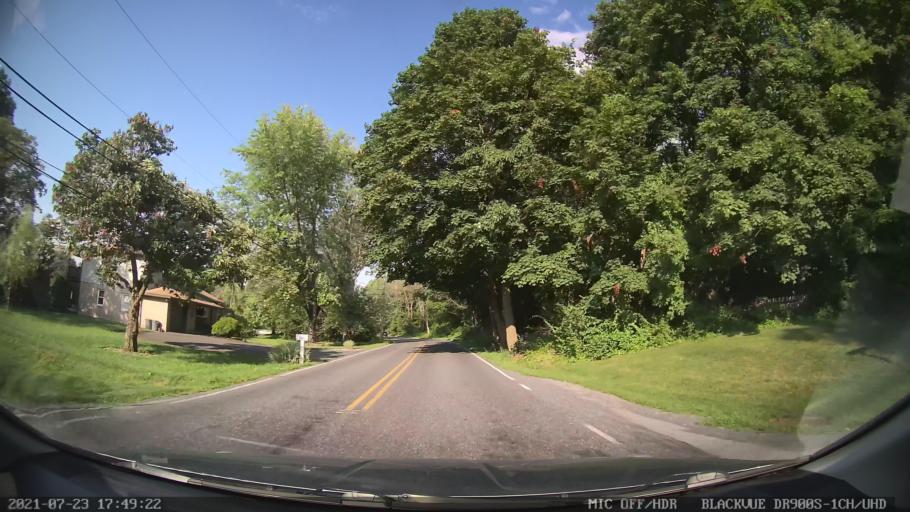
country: US
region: Pennsylvania
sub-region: Berks County
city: Red Lion
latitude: 40.4920
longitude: -75.6088
